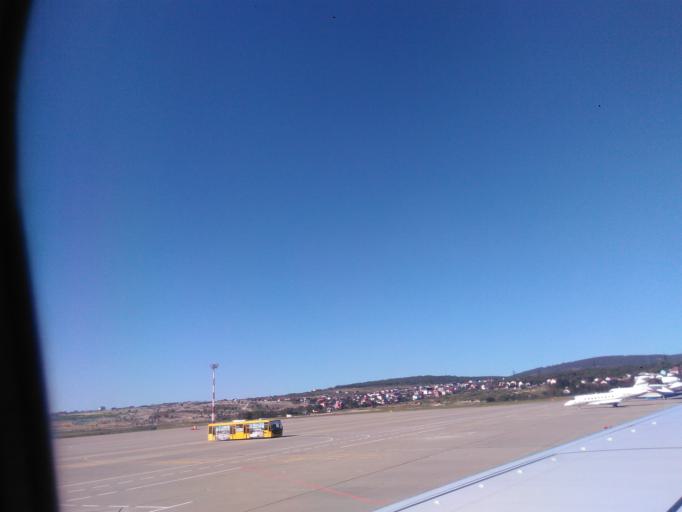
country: RU
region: Krasnodarskiy
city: Gelendzhik
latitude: 44.5942
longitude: 38.0237
